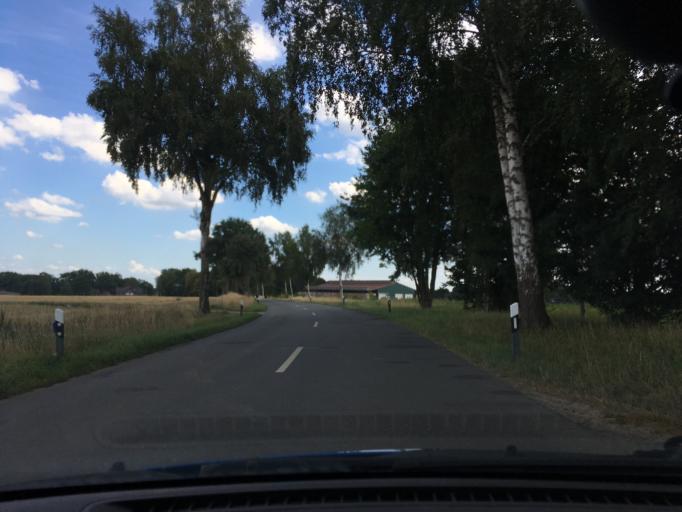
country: DE
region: Lower Saxony
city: Wriedel
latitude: 53.0350
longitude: 10.2746
